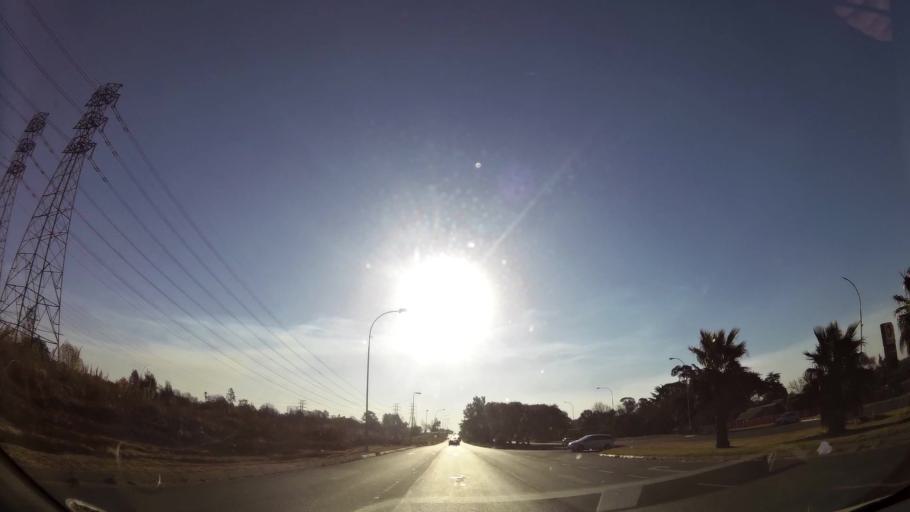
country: ZA
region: Gauteng
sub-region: City of Johannesburg Metropolitan Municipality
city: Roodepoort
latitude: -26.1754
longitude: 27.8785
